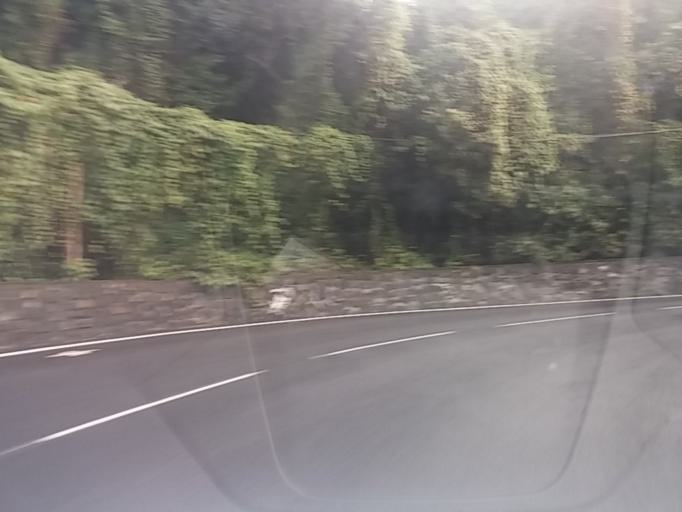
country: RE
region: Reunion
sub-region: Reunion
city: Saint-Denis
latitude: -20.9027
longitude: 55.4208
